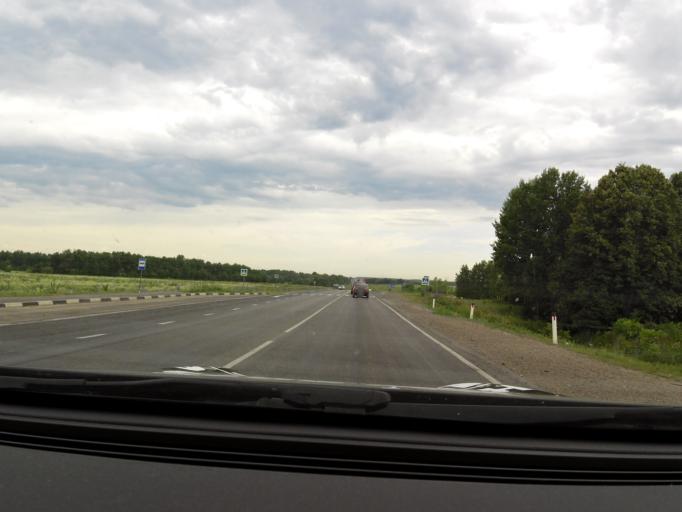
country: RU
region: Bashkortostan
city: Kudeyevskiy
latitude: 54.8172
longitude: 56.7977
